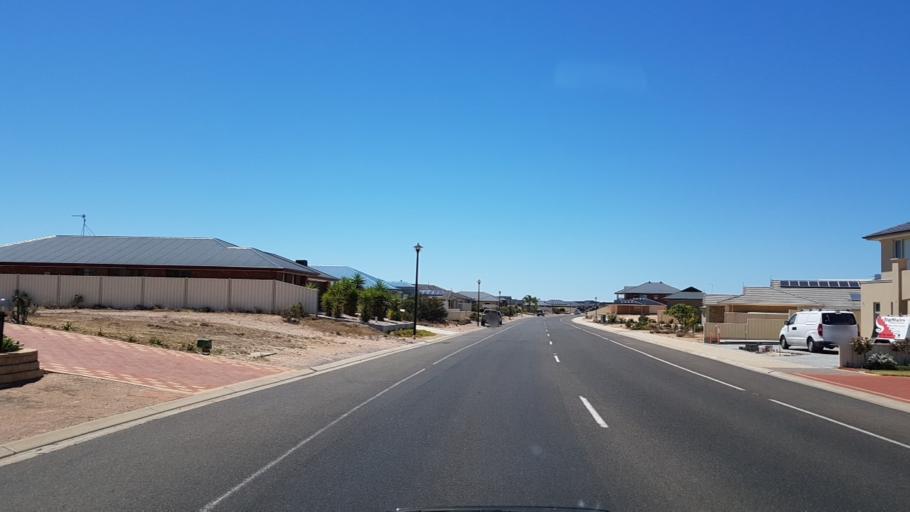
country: AU
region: South Australia
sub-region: Copper Coast
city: Wallaroo
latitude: -33.9172
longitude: 137.6351
